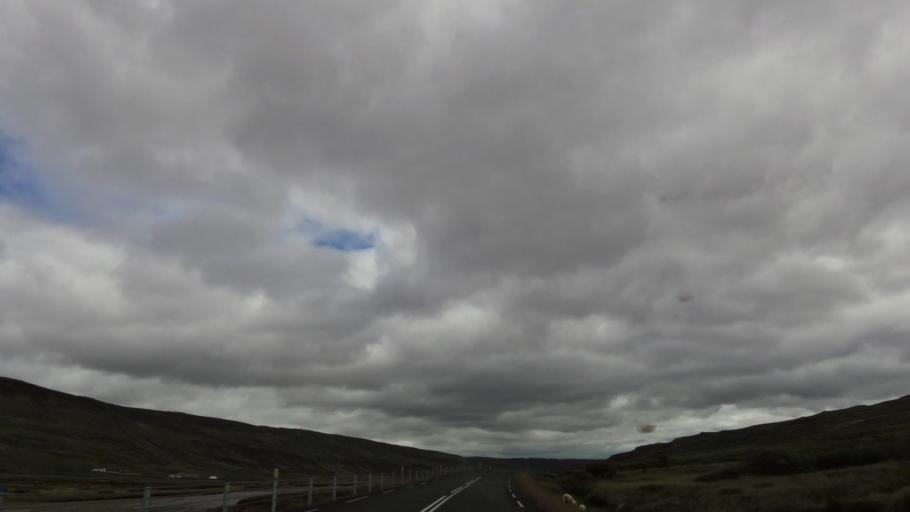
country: IS
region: West
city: Stykkisholmur
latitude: 65.7590
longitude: -21.8570
